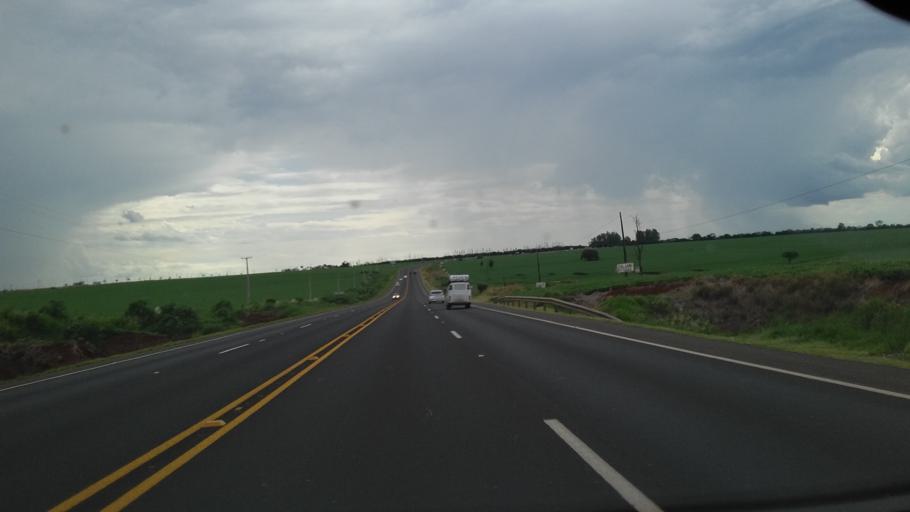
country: BR
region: Parana
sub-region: Arapongas
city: Arapongas
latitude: -23.4125
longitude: -51.4723
